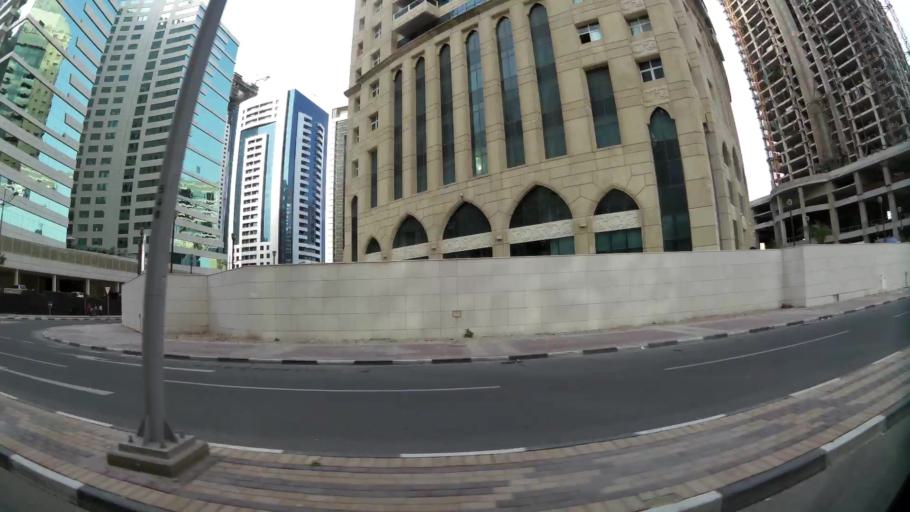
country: QA
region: Baladiyat ad Dawhah
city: Doha
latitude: 25.3249
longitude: 51.5356
